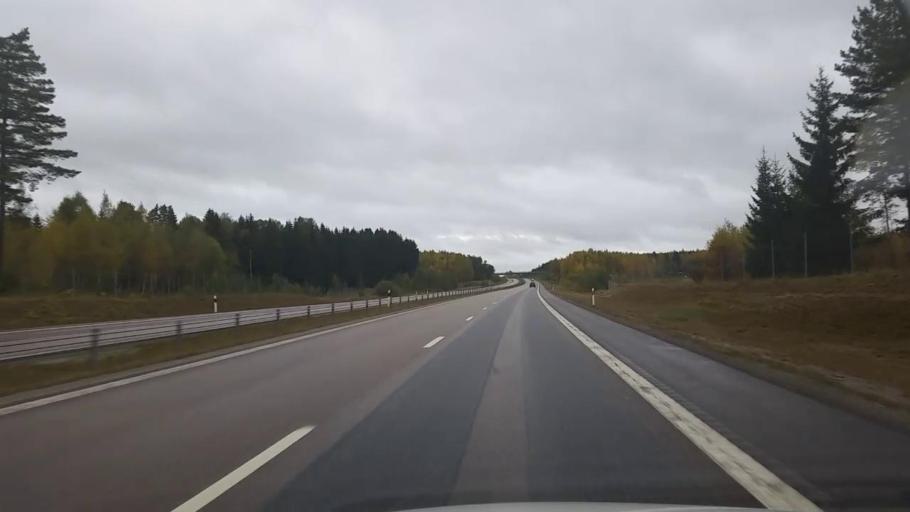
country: SE
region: Uppsala
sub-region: Osthammars Kommun
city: Bjorklinge
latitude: 60.1245
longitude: 17.5468
